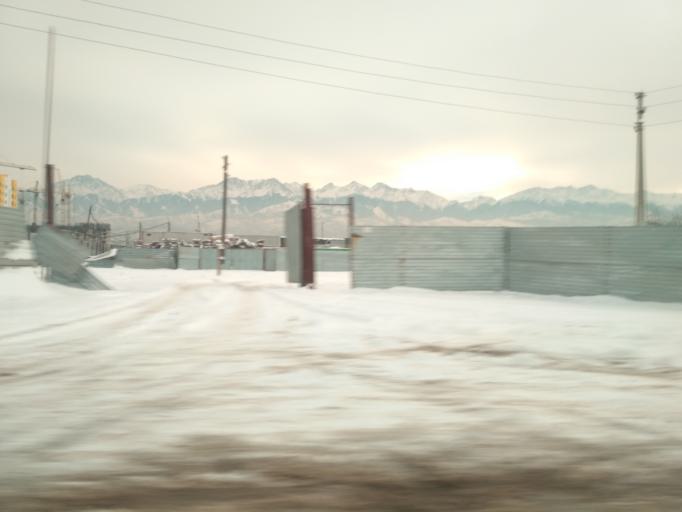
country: KZ
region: Almaty Qalasy
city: Almaty
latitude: 43.2143
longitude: 76.7873
